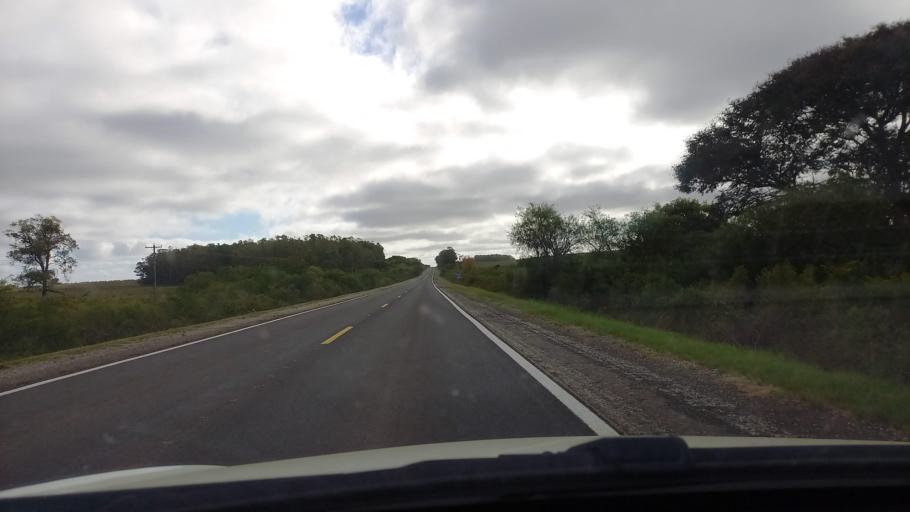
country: BR
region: Rio Grande do Sul
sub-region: Dom Pedrito
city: Dom Pedrito
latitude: -30.9131
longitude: -54.8040
